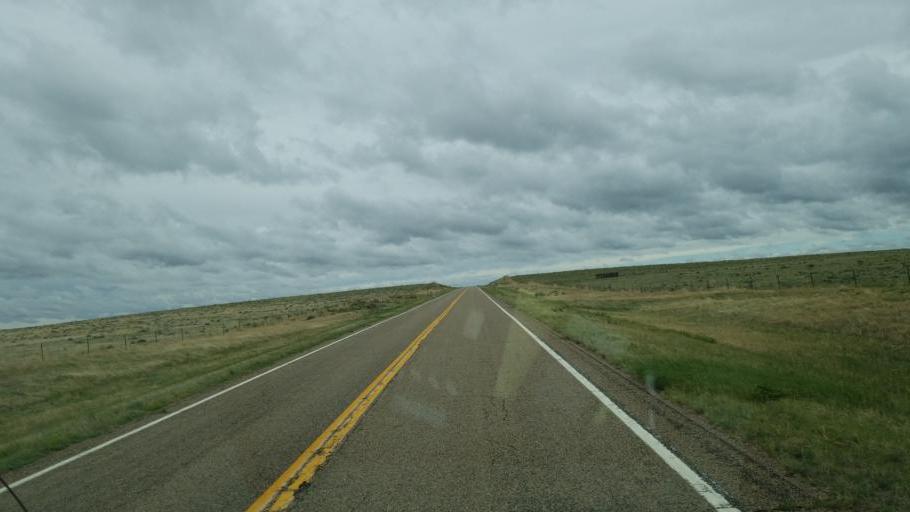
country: US
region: Colorado
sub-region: Lincoln County
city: Hugo
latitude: 38.8506
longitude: -103.5483
